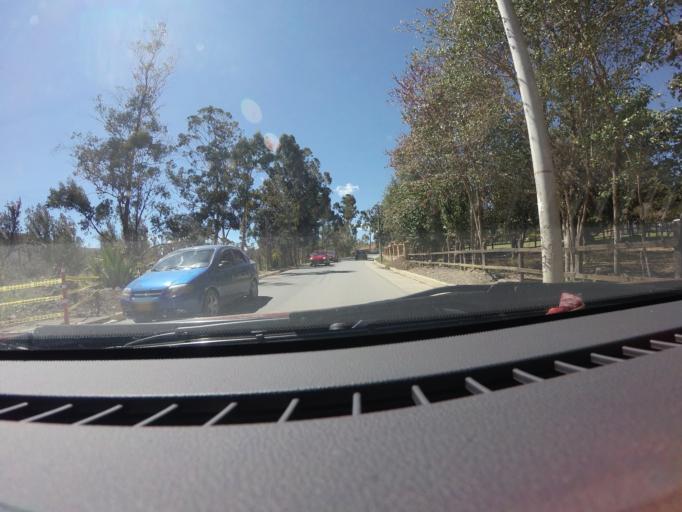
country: CO
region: Boyaca
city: Villa de Leiva
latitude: 5.6298
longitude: -73.5369
